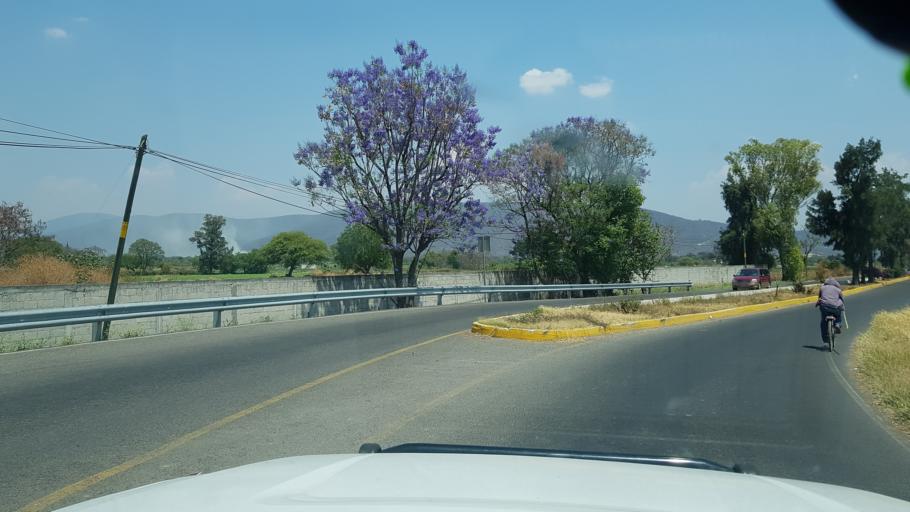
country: MX
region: Puebla
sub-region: Huaquechula
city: Cacaloxuchitl
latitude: 18.7929
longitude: -98.4651
